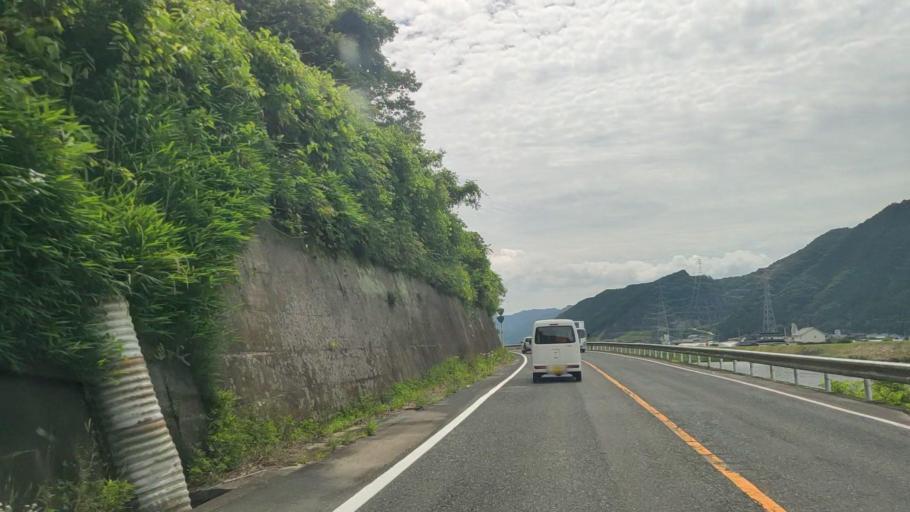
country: JP
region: Okayama
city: Niimi
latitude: 35.0835
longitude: 133.7210
